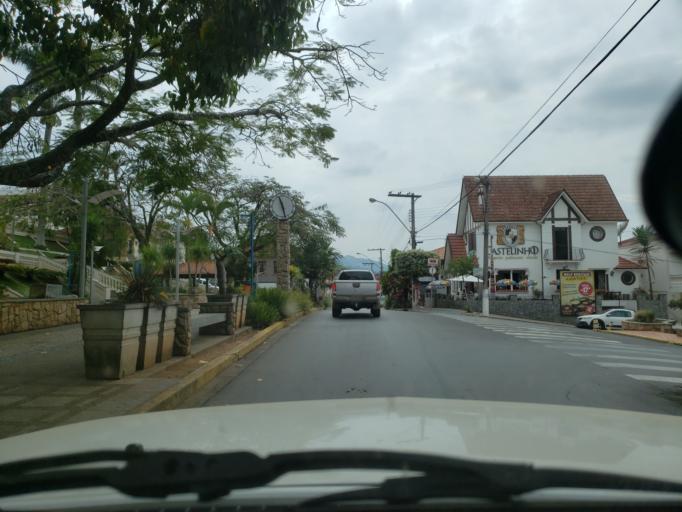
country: BR
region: Minas Gerais
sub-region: Jacutinga
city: Jacutinga
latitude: -22.2859
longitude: -46.6122
